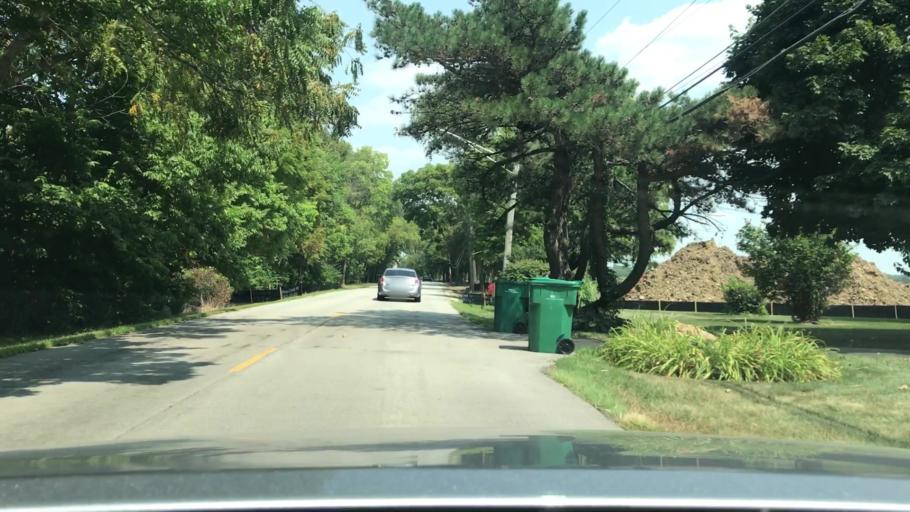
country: US
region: Illinois
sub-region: Will County
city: Plainfield
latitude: 41.5979
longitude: -88.2162
